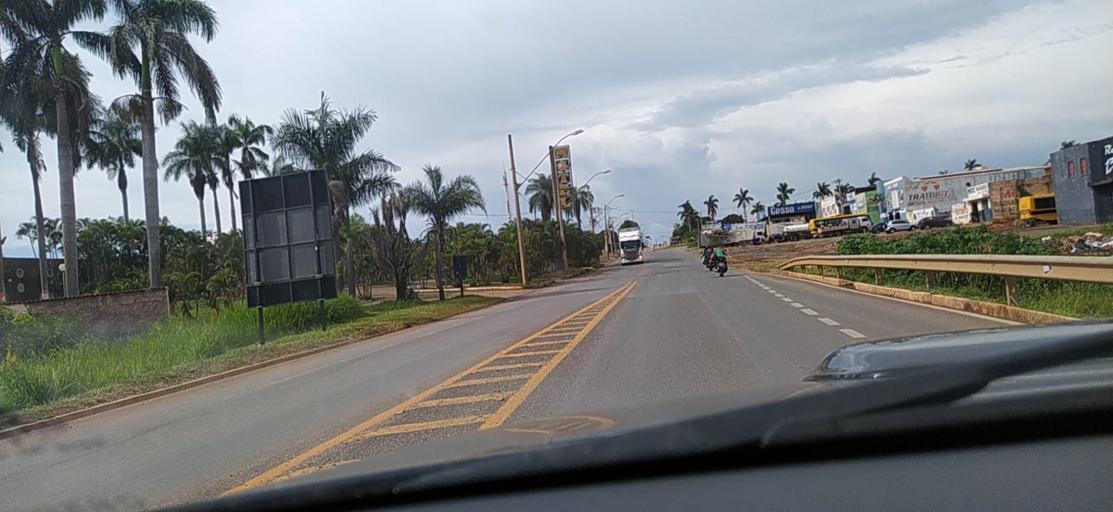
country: BR
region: Minas Gerais
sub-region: Montes Claros
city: Montes Claros
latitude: -16.7484
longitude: -43.8464
